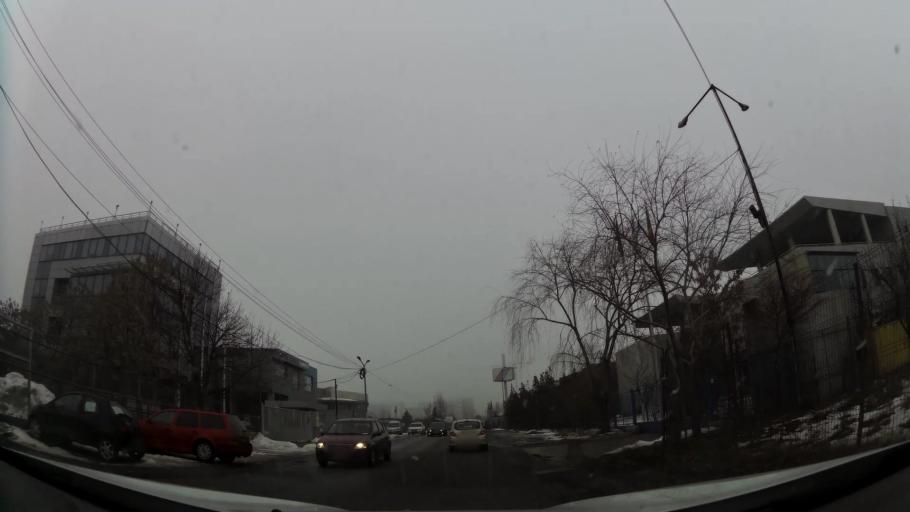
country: RO
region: Ilfov
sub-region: Comuna Chiajna
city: Chiajna
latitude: 44.4378
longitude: 25.9874
